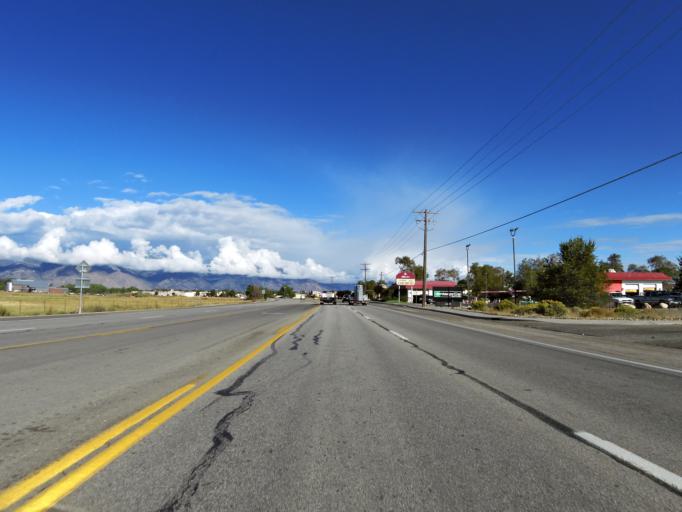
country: US
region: Nevada
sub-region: Douglas County
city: Gardnerville
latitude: 38.9303
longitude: -119.7321
